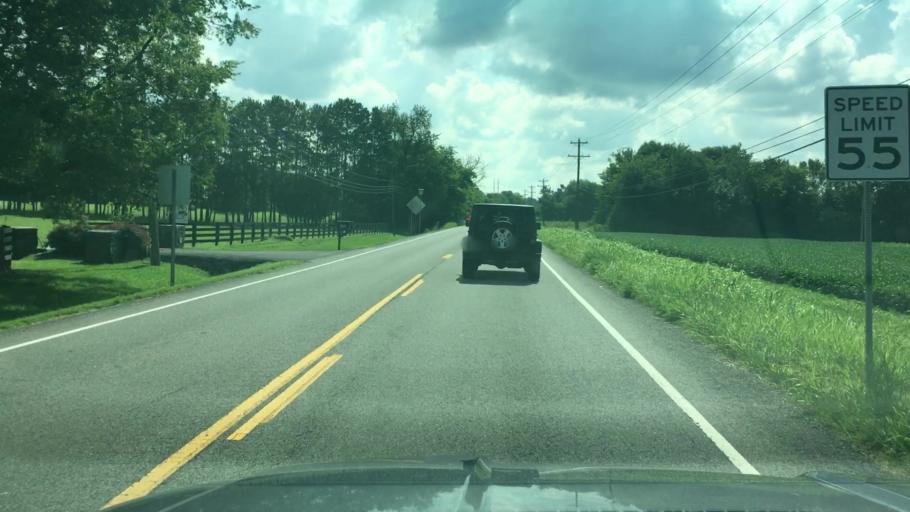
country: US
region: Tennessee
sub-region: Williamson County
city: Nolensville
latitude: 35.8679
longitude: -86.7061
